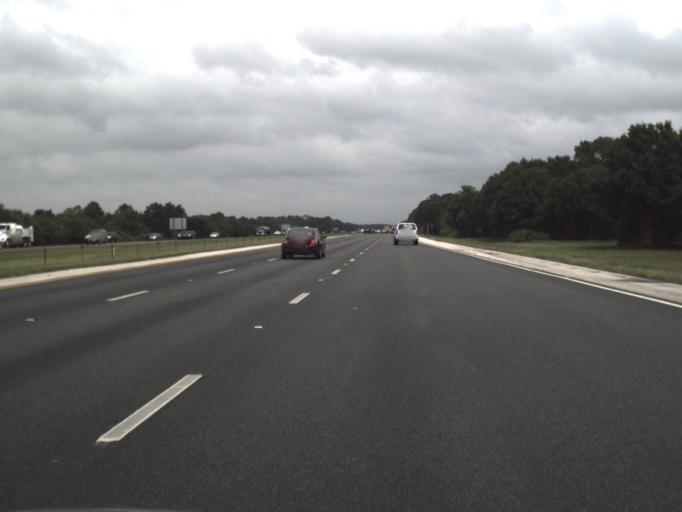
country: US
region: Florida
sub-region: Sarasota County
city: Desoto Lakes
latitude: 27.4464
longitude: -82.4591
